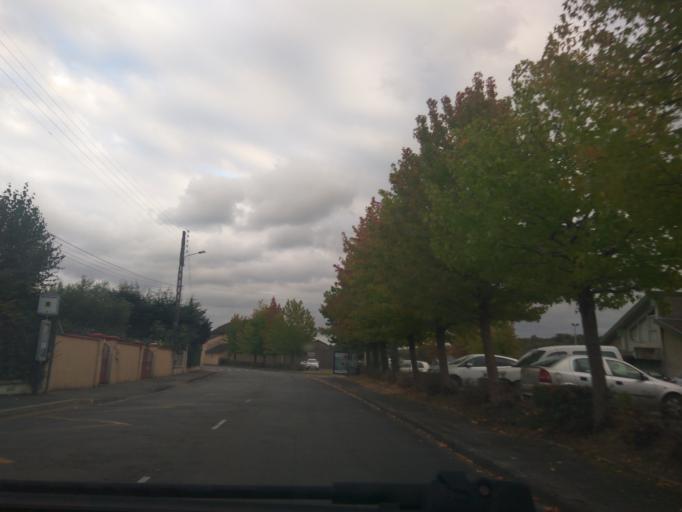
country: FR
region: Aquitaine
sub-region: Departement des Pyrenees-Atlantiques
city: Bizanos
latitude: 43.2918
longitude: -0.3463
